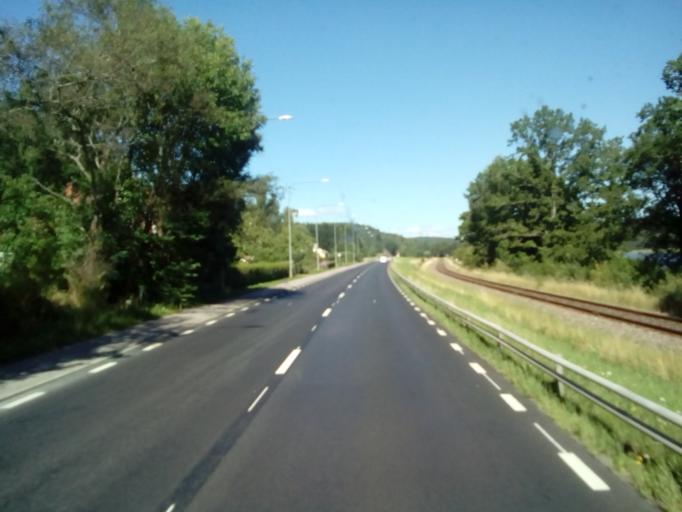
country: SE
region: OEstergoetland
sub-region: Kinda Kommun
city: Kisa
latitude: 58.0049
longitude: 15.6441
